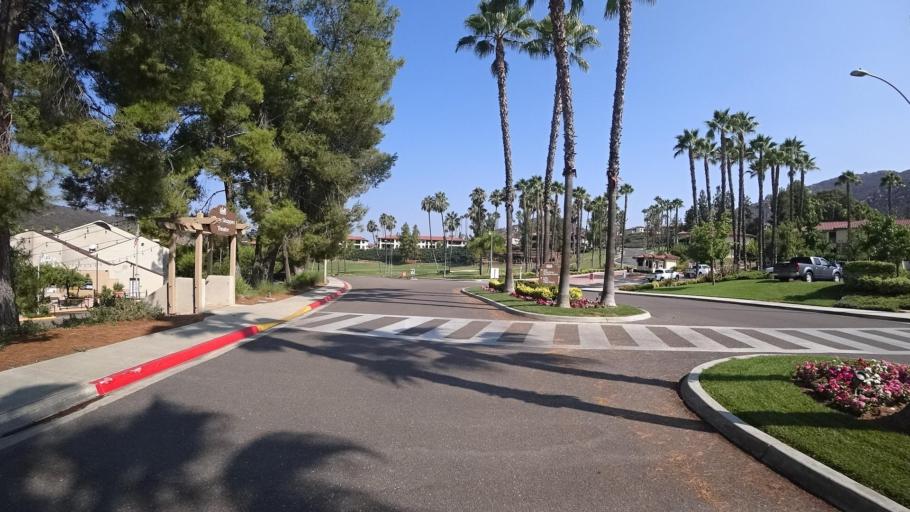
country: US
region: California
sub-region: San Diego County
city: Hidden Meadows
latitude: 33.2324
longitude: -117.1419
